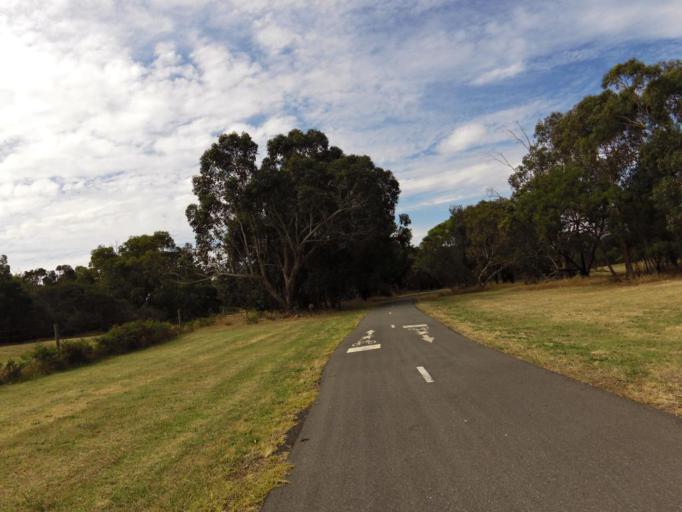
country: AU
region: Victoria
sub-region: Kingston
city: Carrum
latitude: -38.0884
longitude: 145.1371
